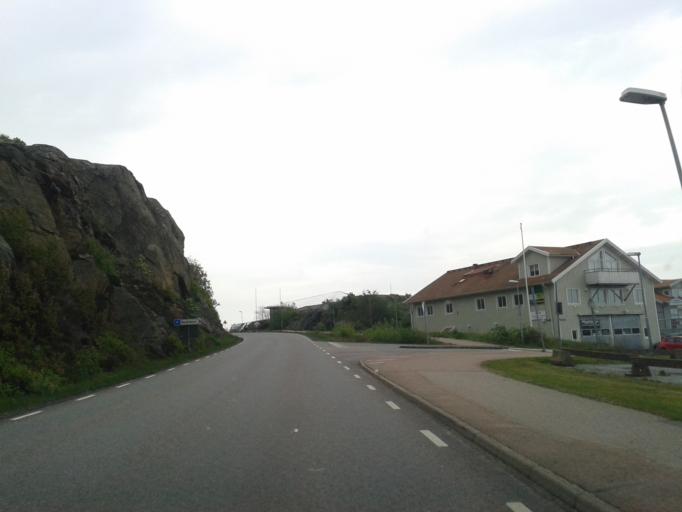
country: SE
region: Vaestra Goetaland
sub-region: Kungalvs Kommun
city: Marstrand
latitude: 57.8882
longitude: 11.6006
